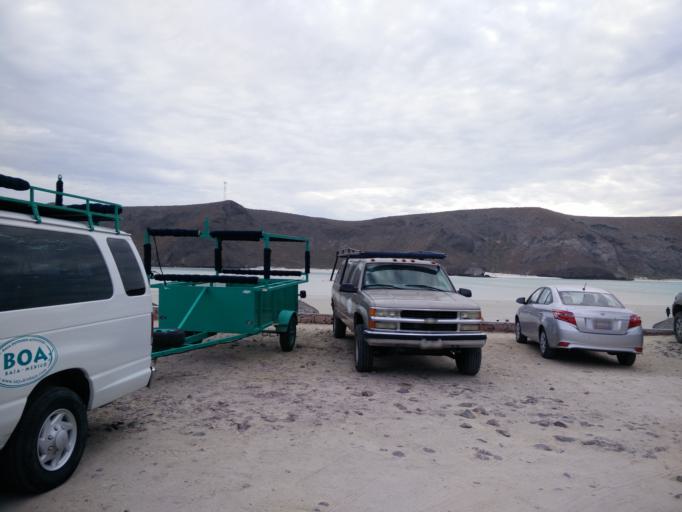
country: MX
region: Baja California Sur
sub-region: La Paz
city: La Paz
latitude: 24.3222
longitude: -110.3244
